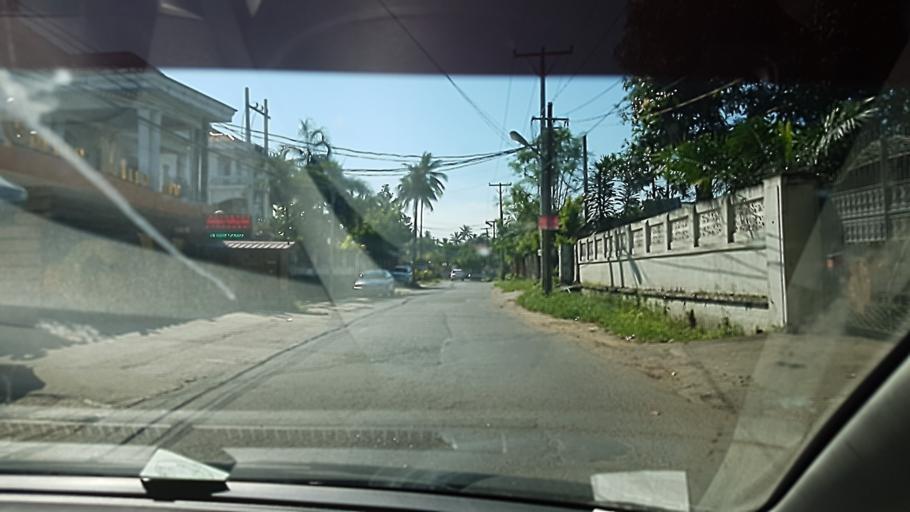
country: MM
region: Yangon
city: Yangon
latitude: 16.8217
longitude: 96.1474
